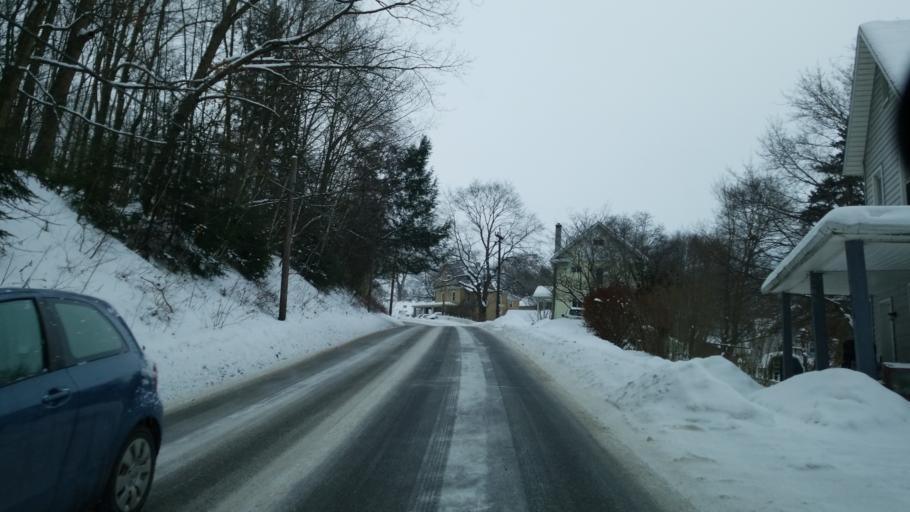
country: US
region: Pennsylvania
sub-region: Clearfield County
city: Clearfield
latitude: 41.0252
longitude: -78.4283
